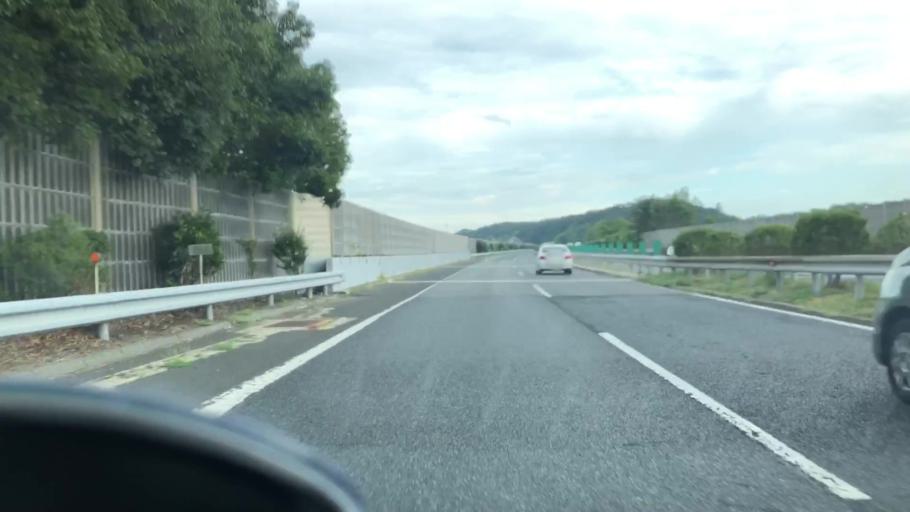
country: JP
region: Hyogo
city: Yashiro
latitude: 34.9062
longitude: 135.0641
